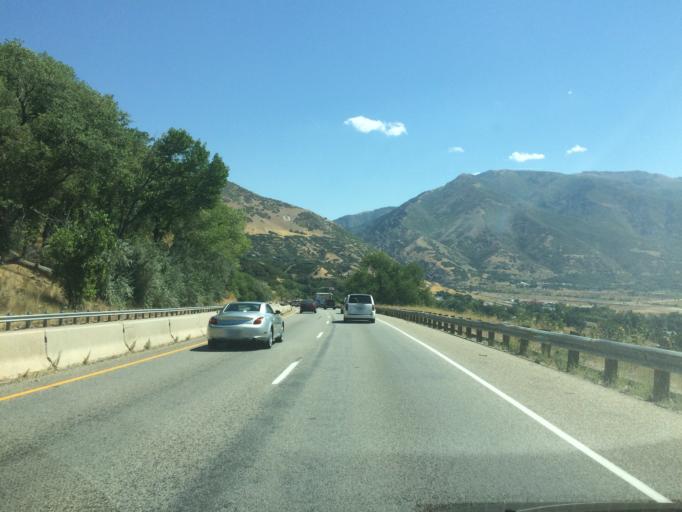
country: US
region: Utah
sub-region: Weber County
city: Uintah
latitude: 41.1482
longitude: -111.9301
